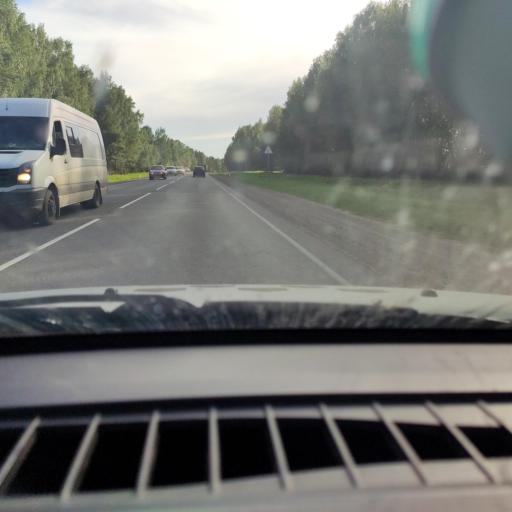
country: RU
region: Kirov
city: Vakhrushi
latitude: 58.6438
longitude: 49.8554
